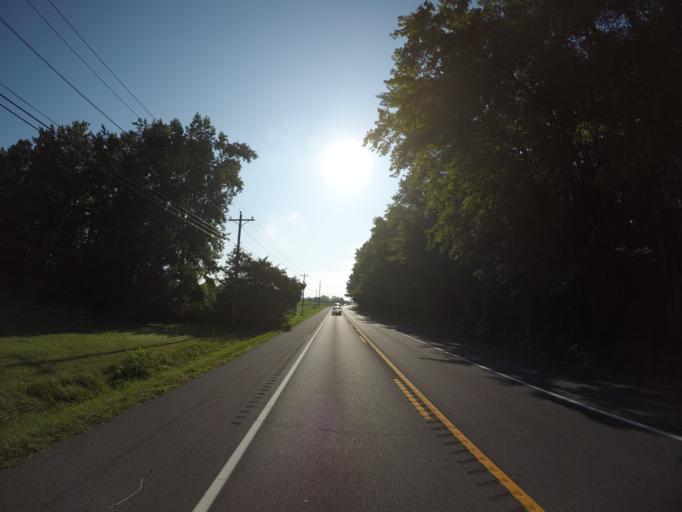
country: US
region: Delaware
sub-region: Sussex County
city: Georgetown
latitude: 38.6983
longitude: -75.4358
